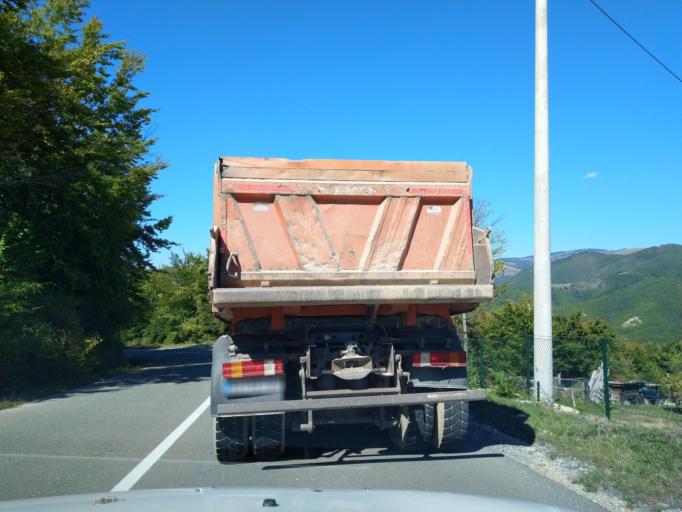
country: RS
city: Sokolovica
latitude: 43.2511
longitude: 20.2458
